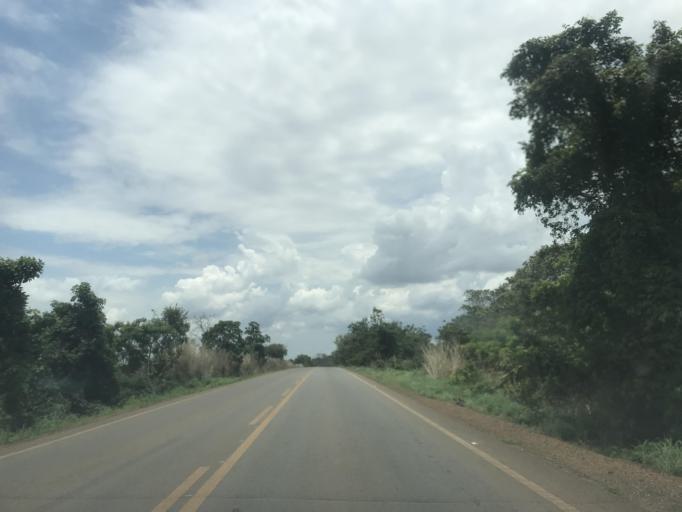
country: BR
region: Goias
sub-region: Vianopolis
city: Vianopolis
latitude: -16.7379
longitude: -48.4473
